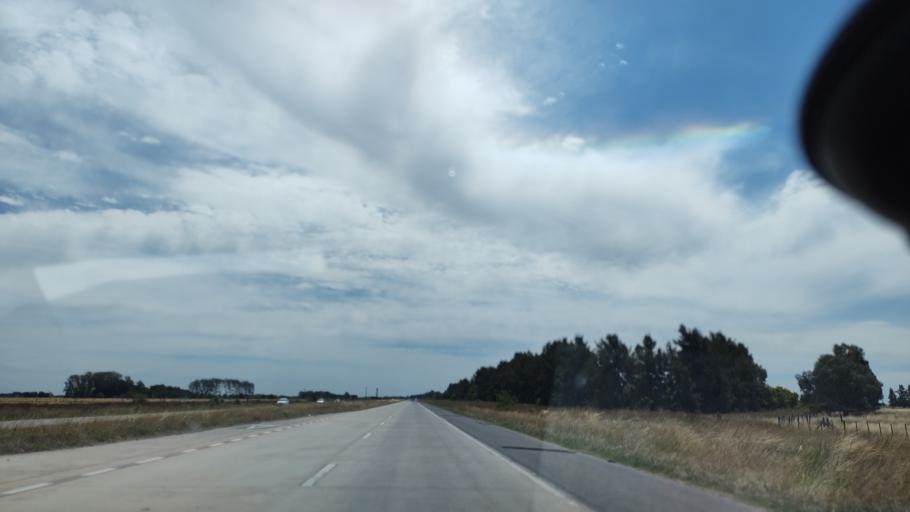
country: AR
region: Buenos Aires
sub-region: Partido de Brandsen
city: Brandsen
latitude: -35.0449
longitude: -58.1574
